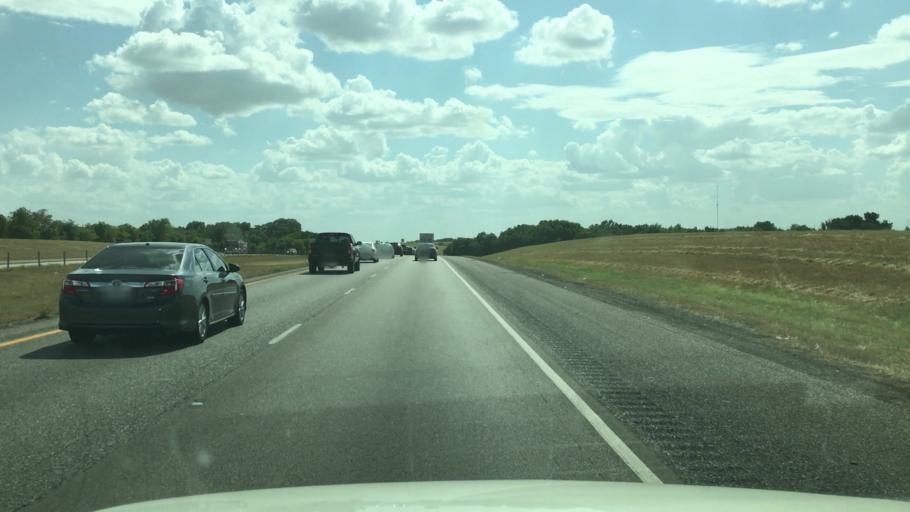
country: US
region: Texas
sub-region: Ellis County
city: Plum Grove
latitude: 32.1129
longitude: -96.9956
